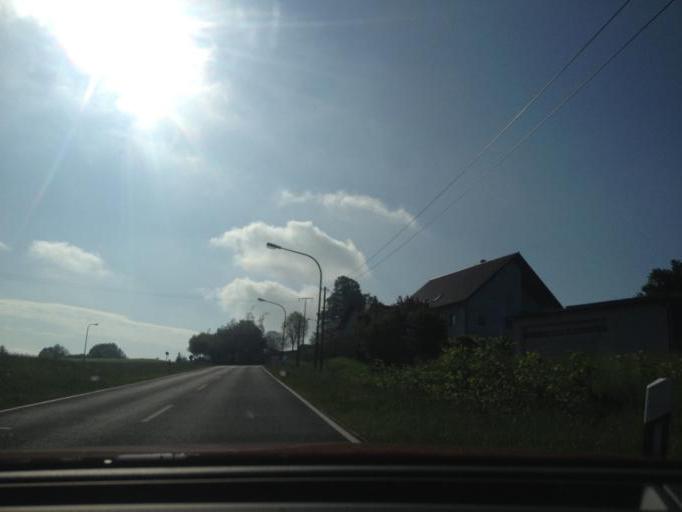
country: DE
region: Bavaria
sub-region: Upper Franconia
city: Prebitz
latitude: 49.7756
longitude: 11.6586
